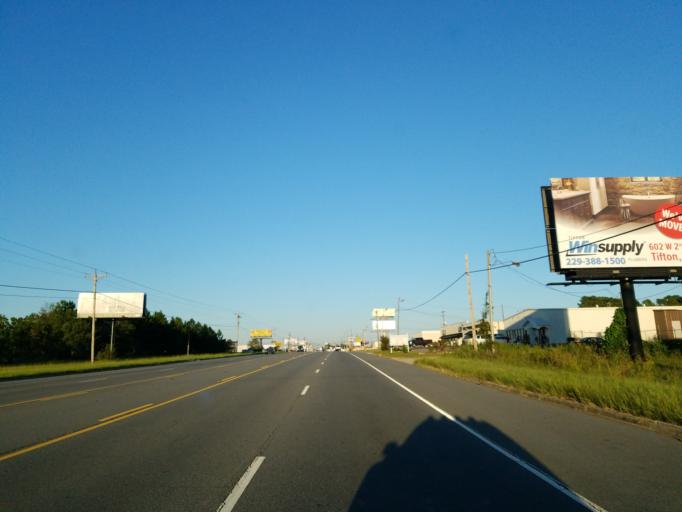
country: US
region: Georgia
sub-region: Tift County
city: Unionville
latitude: 31.4432
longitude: -83.5511
